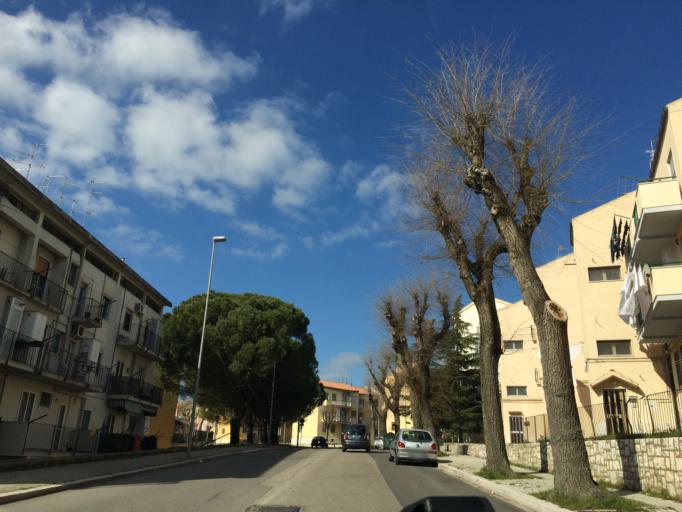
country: IT
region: Basilicate
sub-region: Provincia di Matera
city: Matera
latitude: 40.6650
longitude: 16.5929
